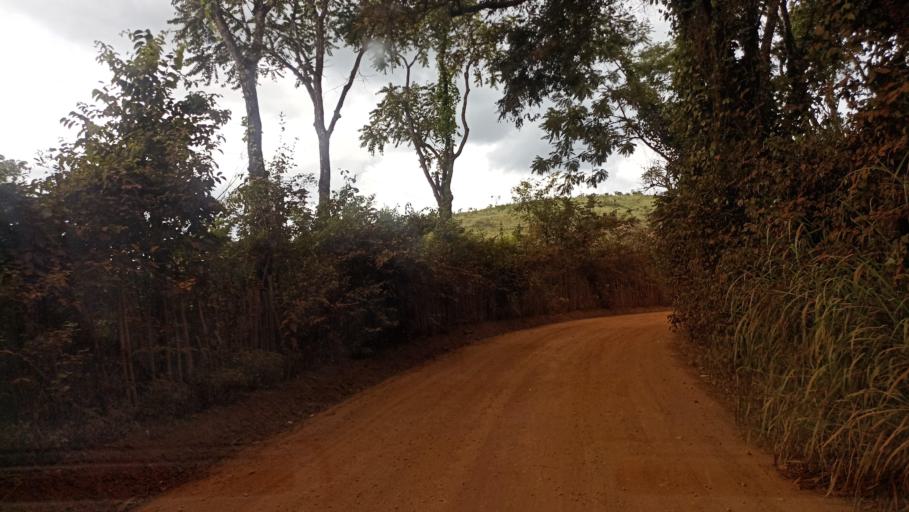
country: BR
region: Minas Gerais
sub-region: Itabirito
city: Itabirito
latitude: -20.3619
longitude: -43.7672
